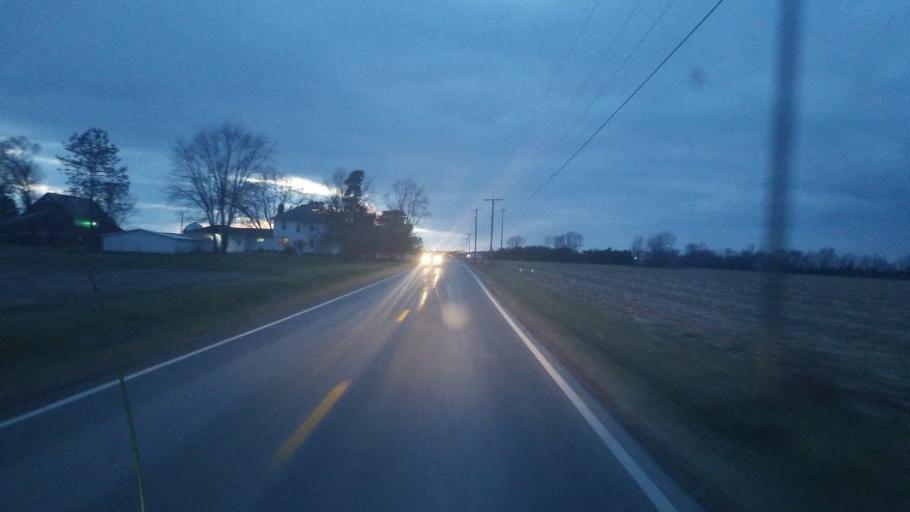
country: US
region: Ohio
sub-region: Marion County
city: Prospect
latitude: 40.4343
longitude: -83.0783
